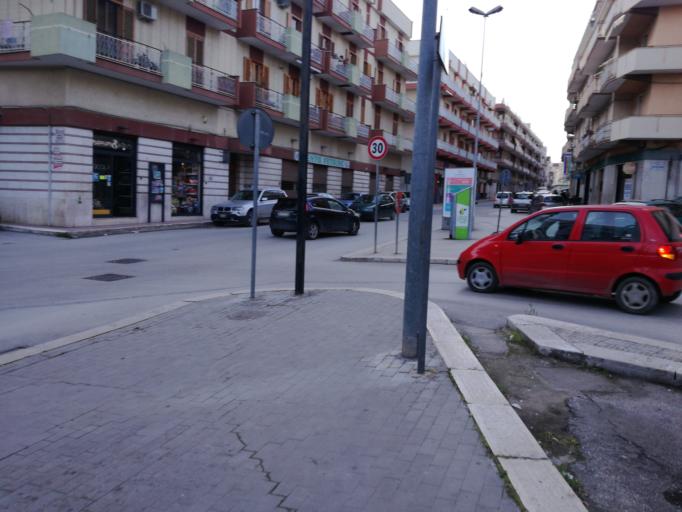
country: IT
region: Apulia
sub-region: Provincia di Bari
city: Corato
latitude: 41.1475
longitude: 16.4157
